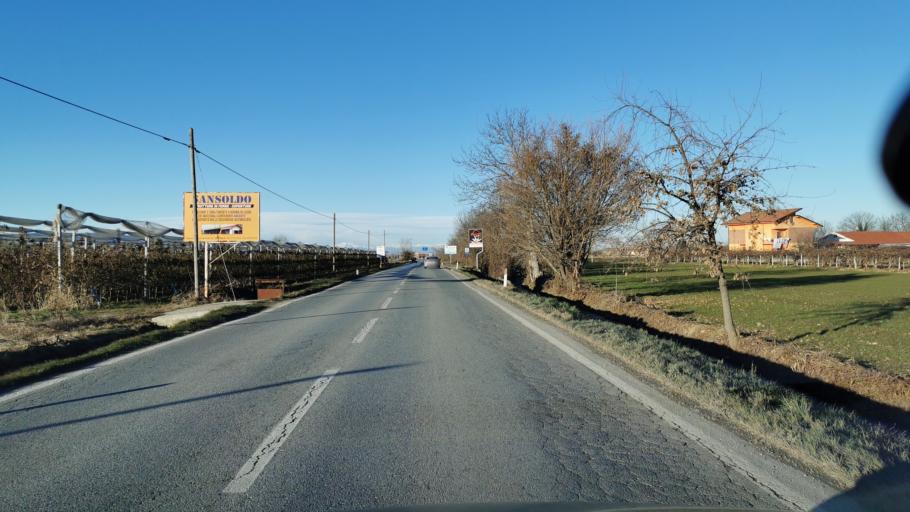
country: IT
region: Piedmont
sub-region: Provincia di Cuneo
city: Roata Rossi
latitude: 44.4333
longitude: 7.5442
